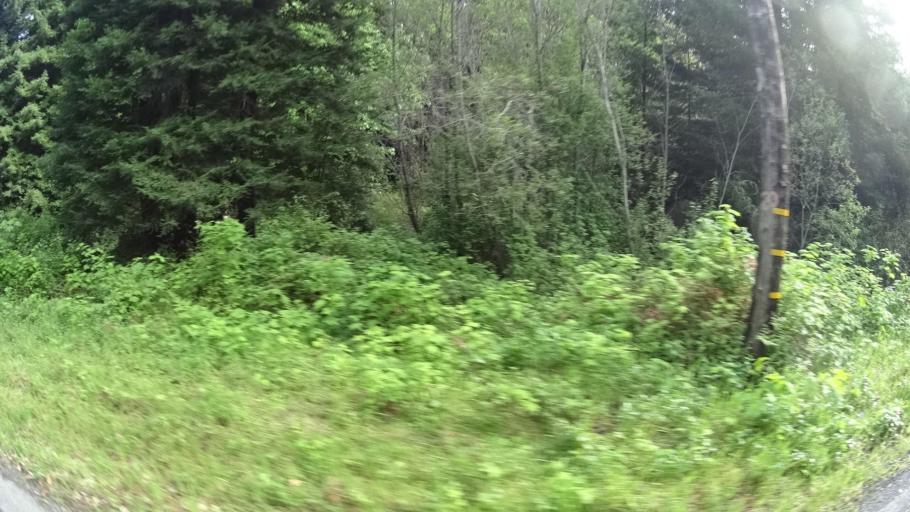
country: US
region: California
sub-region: Humboldt County
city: Redway
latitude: 40.3405
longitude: -123.8767
